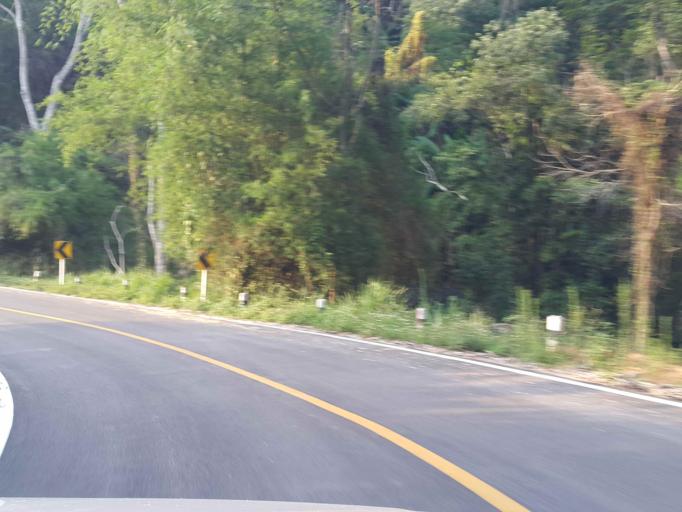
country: TH
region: Chiang Mai
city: Mae On
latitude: 18.9636
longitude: 99.3289
